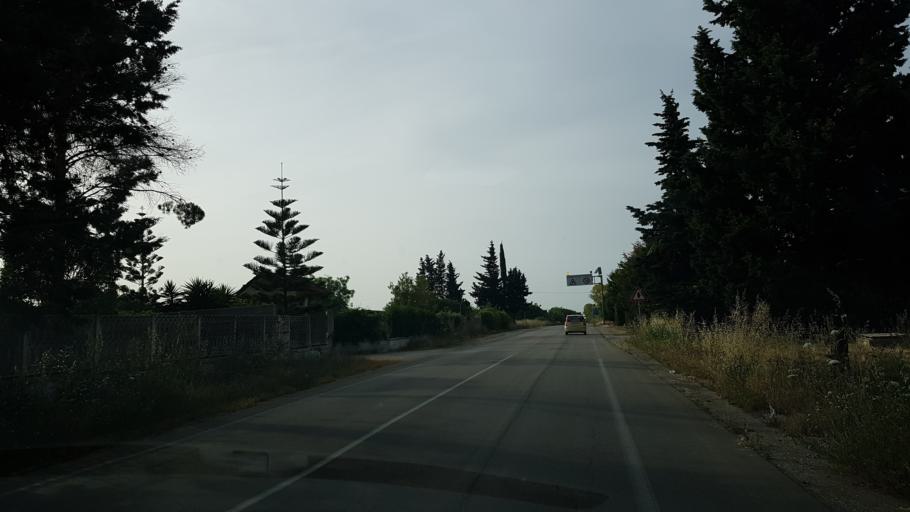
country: IT
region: Apulia
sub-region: Provincia di Brindisi
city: Tuturano
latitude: 40.5468
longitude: 17.9770
